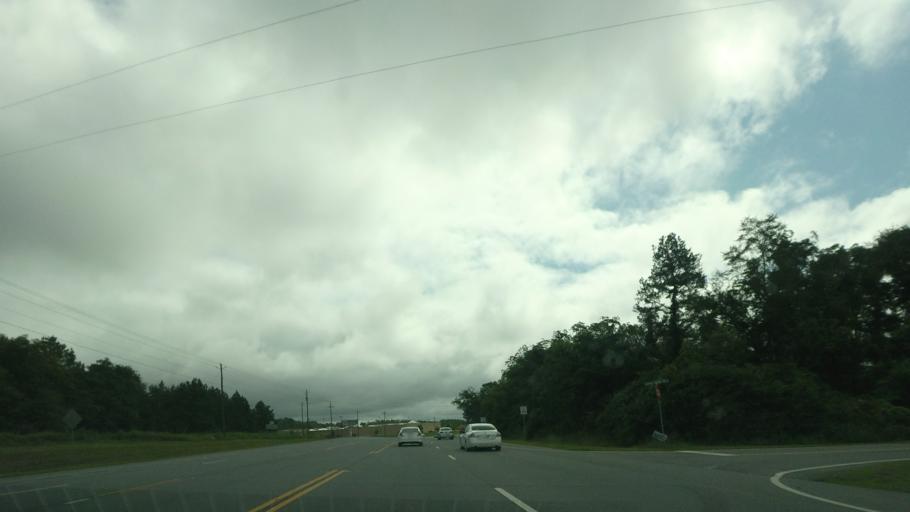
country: US
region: Georgia
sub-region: Laurens County
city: Dublin
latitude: 32.5507
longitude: -82.9770
